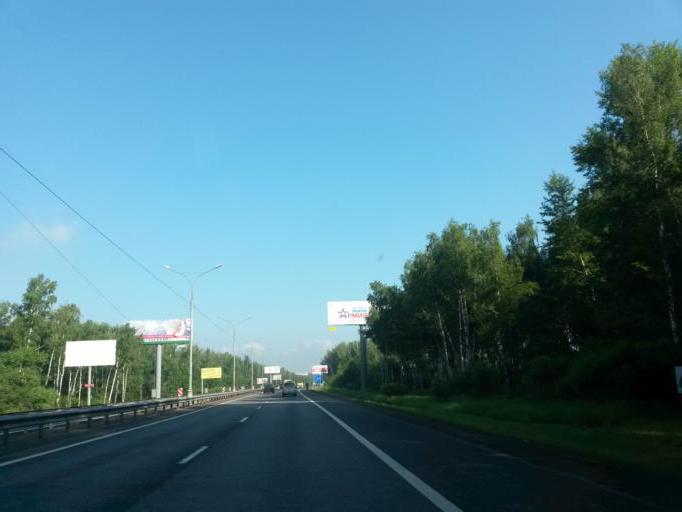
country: RU
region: Moskovskaya
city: Petrovskaya
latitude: 55.5519
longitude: 37.7873
